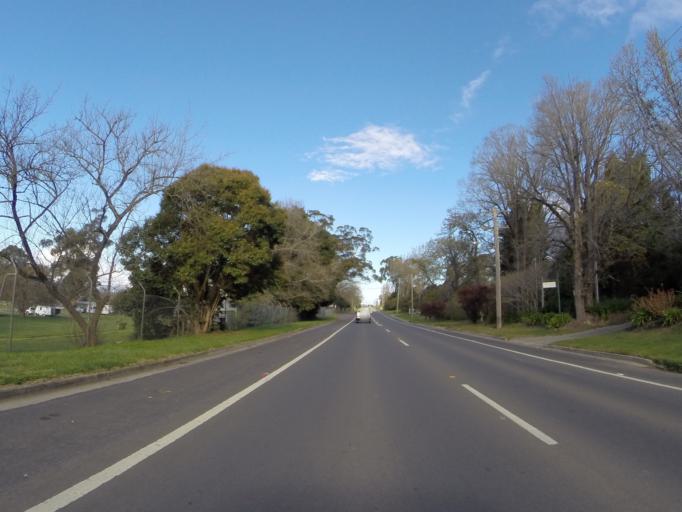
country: AU
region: New South Wales
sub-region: Wingecarribee
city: Moss Vale
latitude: -34.5482
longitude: 150.3823
